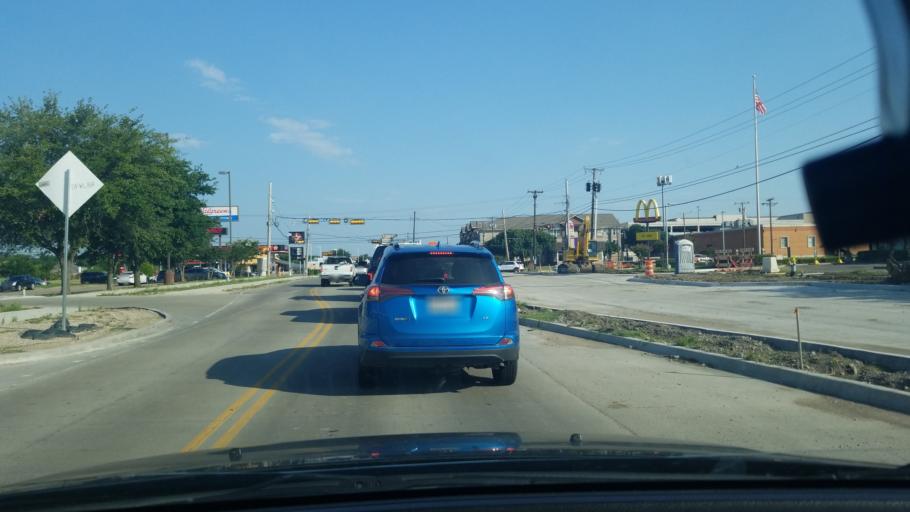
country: US
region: Texas
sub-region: Dallas County
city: Mesquite
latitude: 32.8230
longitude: -96.6455
